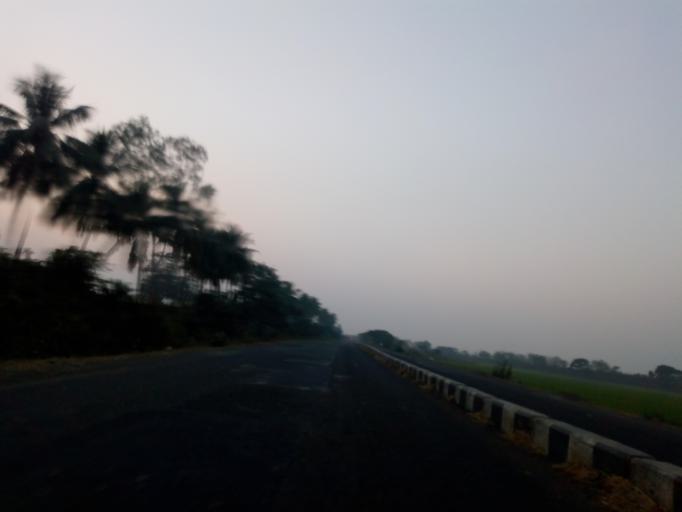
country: IN
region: Andhra Pradesh
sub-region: West Godavari
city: Tadepallegudem
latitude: 16.8227
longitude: 81.4673
